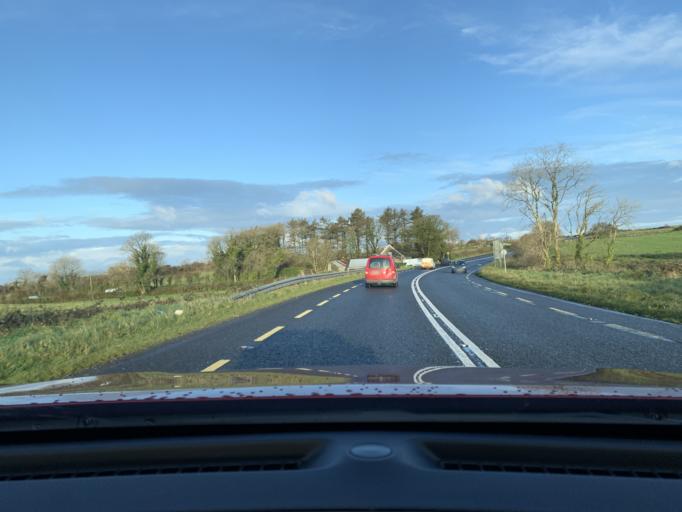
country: IE
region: Connaught
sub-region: Sligo
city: Sligo
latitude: 54.3618
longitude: -8.5258
